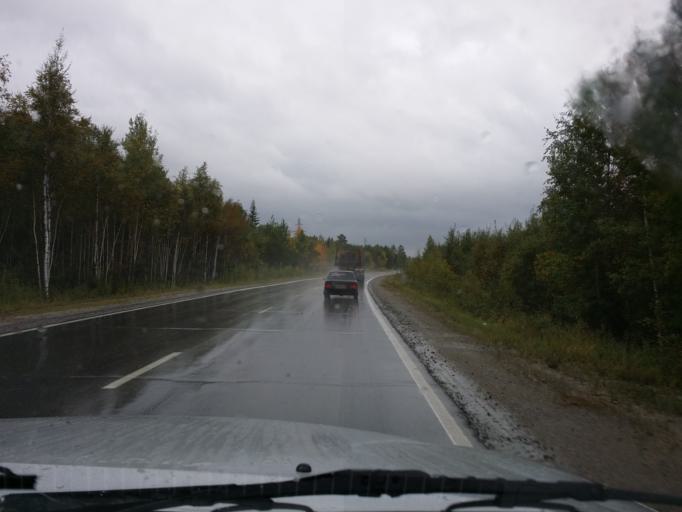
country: RU
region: Khanty-Mansiyskiy Avtonomnyy Okrug
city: Megion
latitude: 61.1439
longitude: 75.7569
